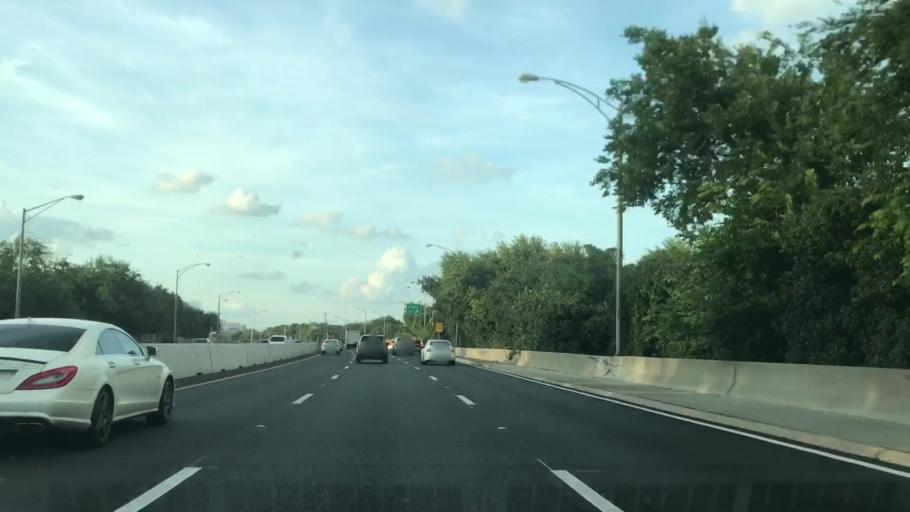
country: US
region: Texas
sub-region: Dallas County
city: University Park
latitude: 32.8912
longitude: -96.8085
